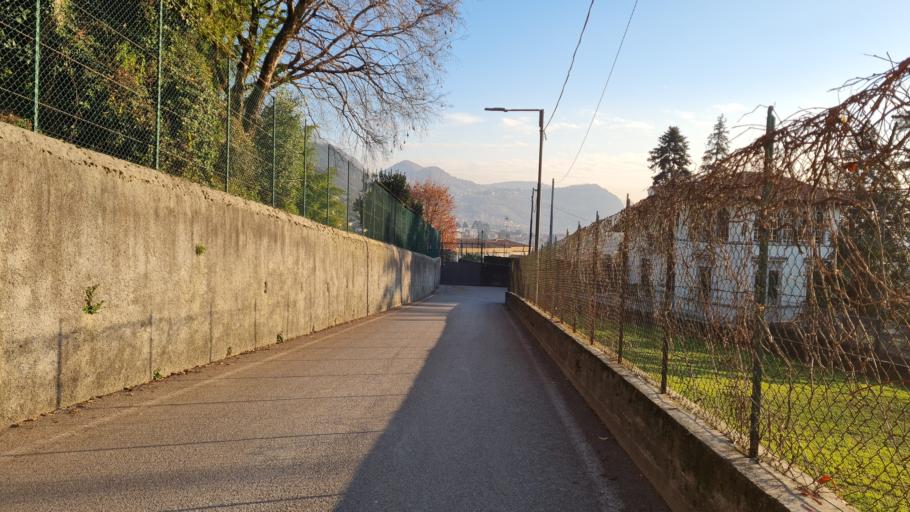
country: IT
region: Lombardy
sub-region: Provincia di Lecco
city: Vercurago
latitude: 45.8049
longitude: 9.4313
